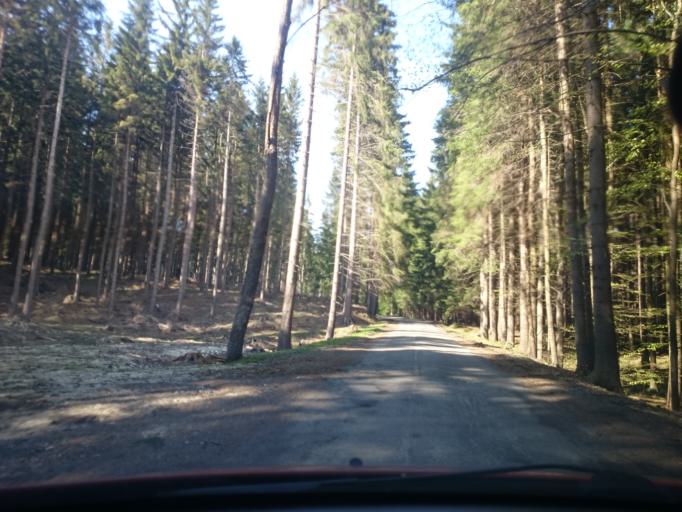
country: PL
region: Lower Silesian Voivodeship
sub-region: Powiat klodzki
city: Polanica-Zdroj
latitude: 50.3048
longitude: 16.4987
